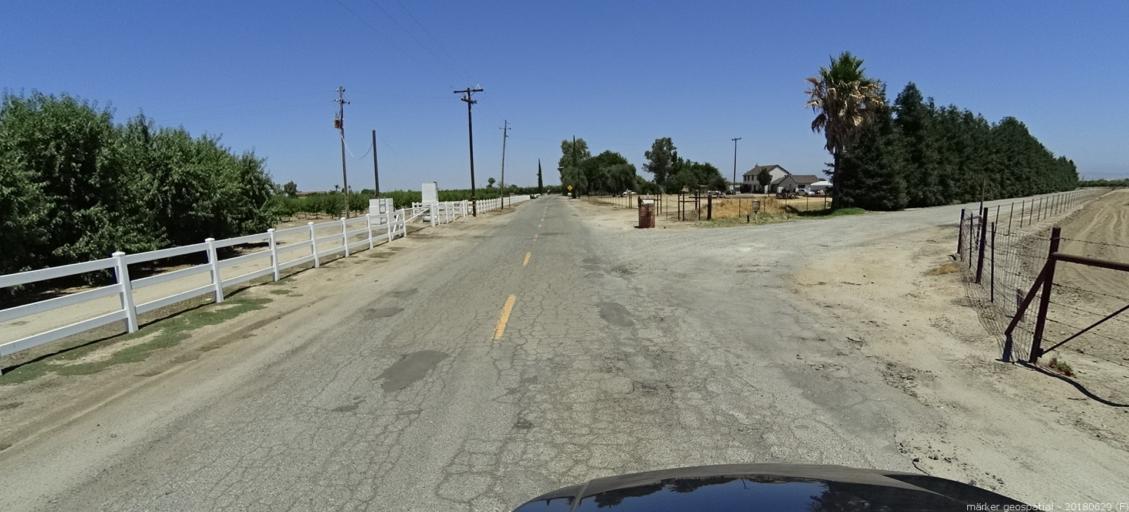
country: US
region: California
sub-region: Madera County
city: Parksdale
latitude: 37.0079
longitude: -119.9912
